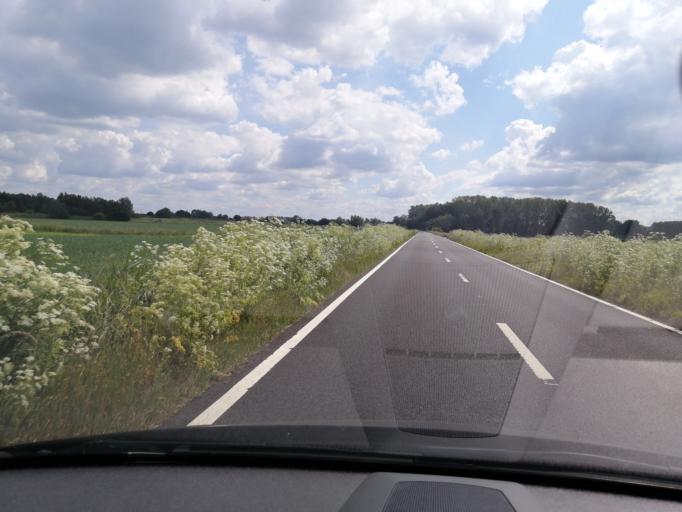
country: GB
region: England
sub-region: Cambridgeshire
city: Yaxley
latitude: 52.4856
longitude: -0.2430
